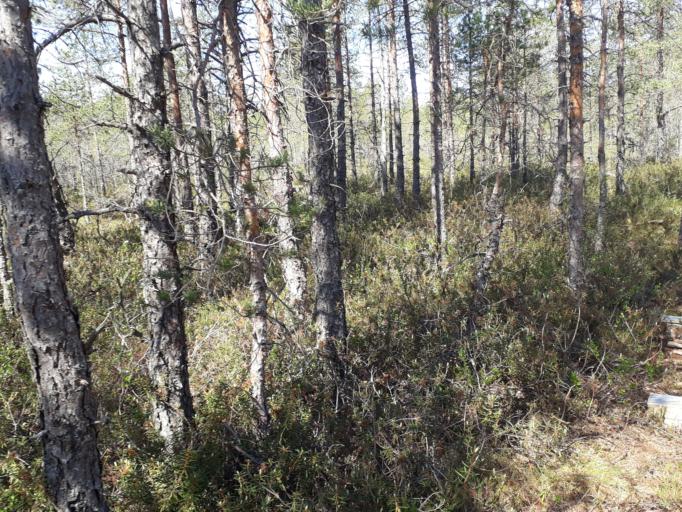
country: EE
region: Harju
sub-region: Loksa linn
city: Loksa
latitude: 59.4780
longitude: 25.6655
